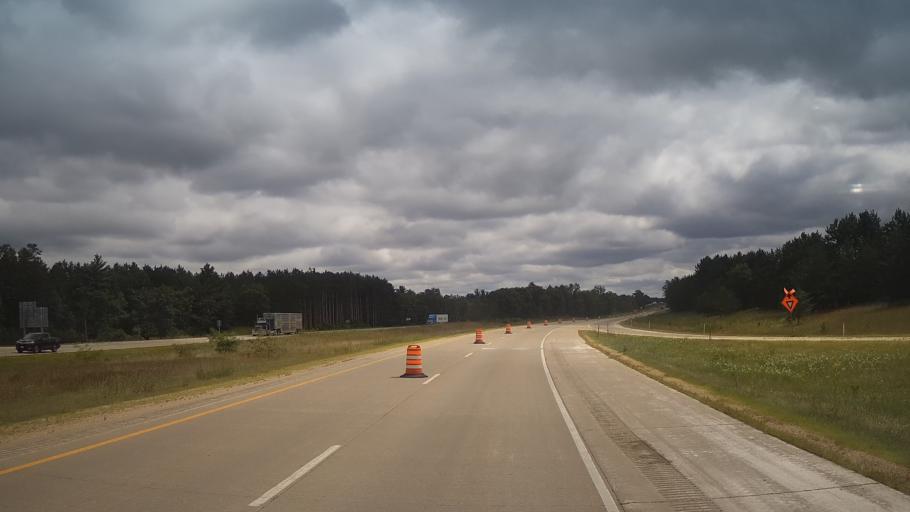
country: US
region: Wisconsin
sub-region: Monroe County
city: Sparta
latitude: 43.9429
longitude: -90.7601
